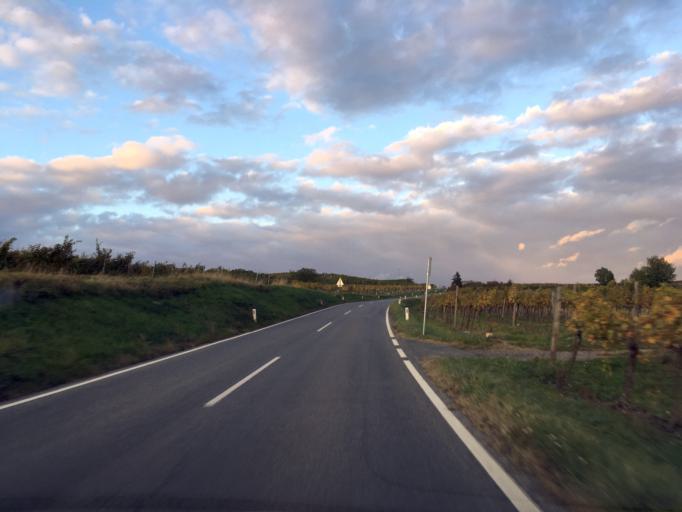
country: AT
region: Lower Austria
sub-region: Politischer Bezirk Baden
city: Pfaffstatten
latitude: 48.0253
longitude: 16.2592
